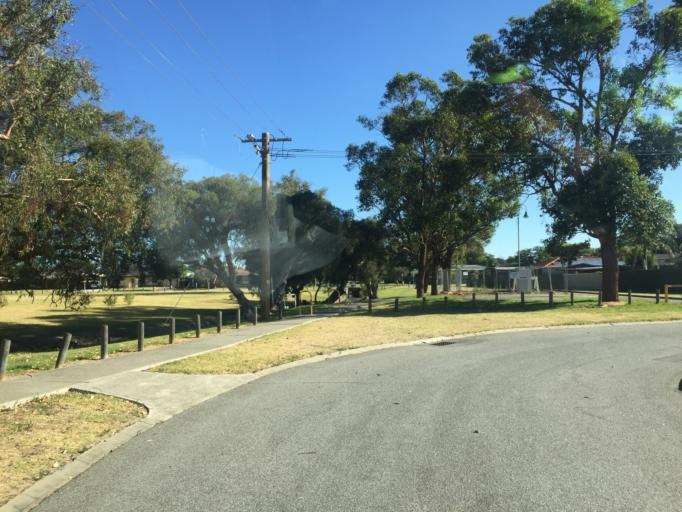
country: AU
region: Western Australia
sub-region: Canning
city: East Cannington
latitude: -32.0149
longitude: 115.9690
